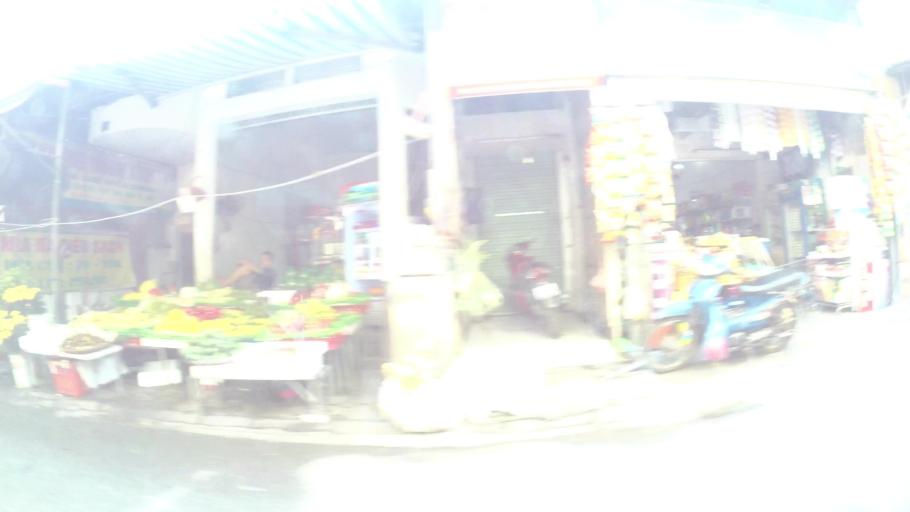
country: VN
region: Ha Noi
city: Thanh Xuan
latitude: 20.9938
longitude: 105.8172
